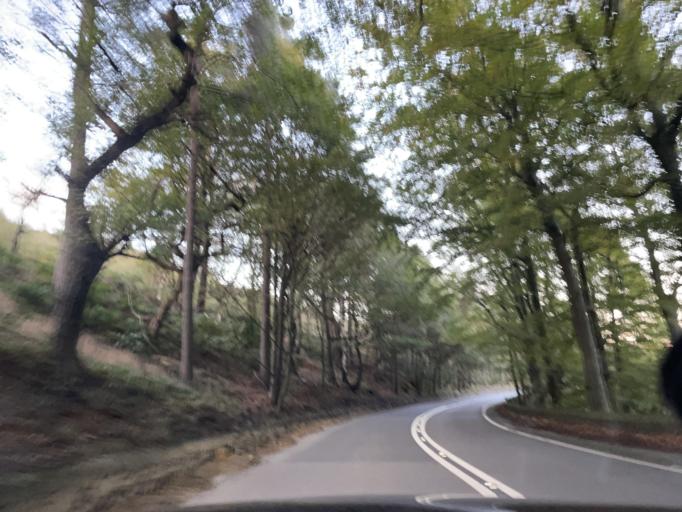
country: GB
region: England
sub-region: Derbyshire
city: Glossop
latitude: 53.4861
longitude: -1.9016
